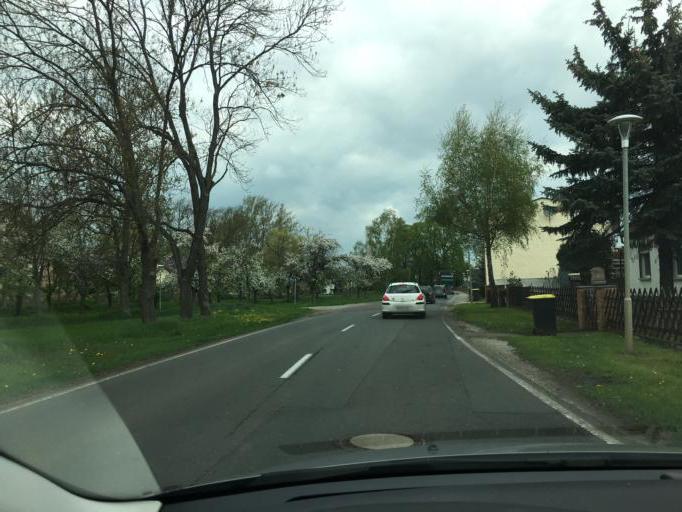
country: DE
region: Saxony-Anhalt
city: Giersleben
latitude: 51.7783
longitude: 11.5842
